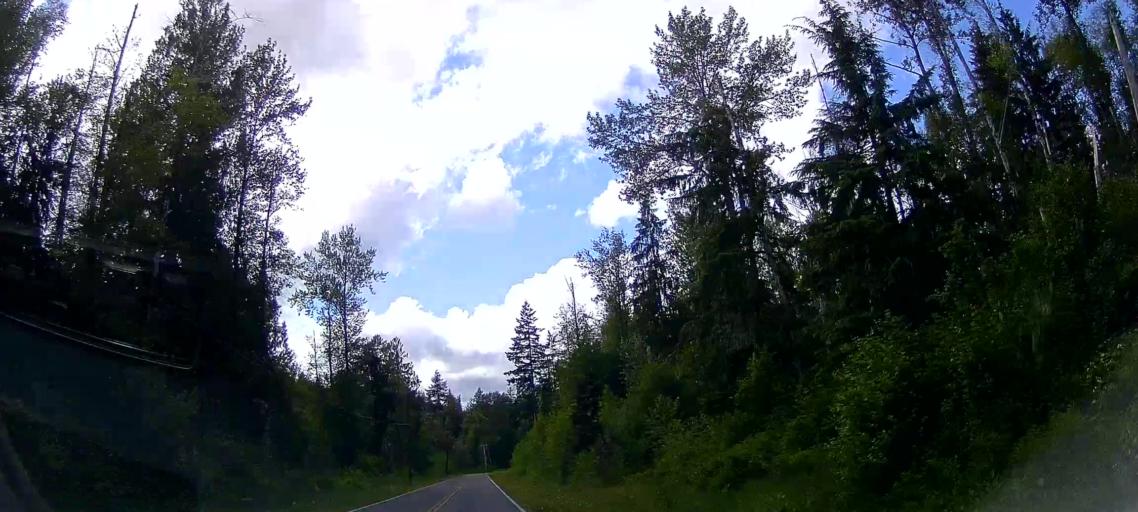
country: US
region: Washington
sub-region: Skagit County
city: Sedro-Woolley
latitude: 48.6718
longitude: -122.1500
